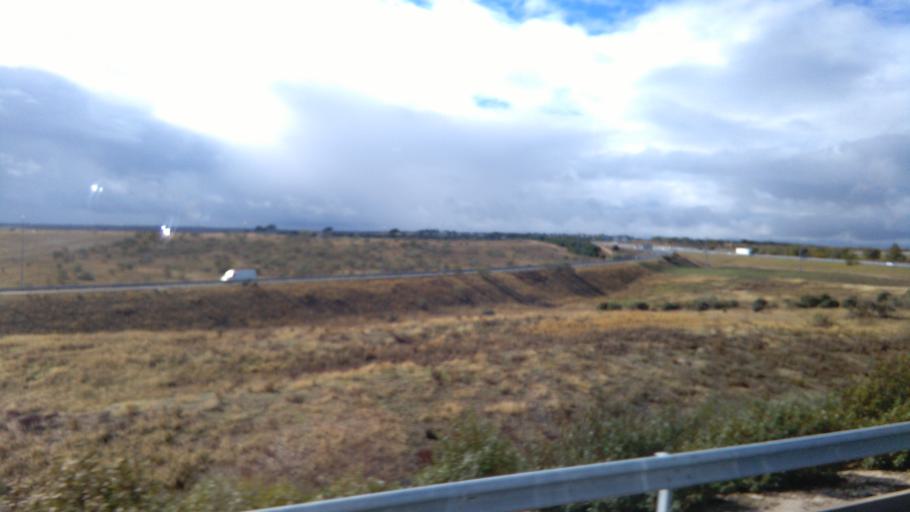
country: ES
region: Madrid
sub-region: Provincia de Madrid
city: Navalcarnero
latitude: 40.2674
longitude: -4.0345
